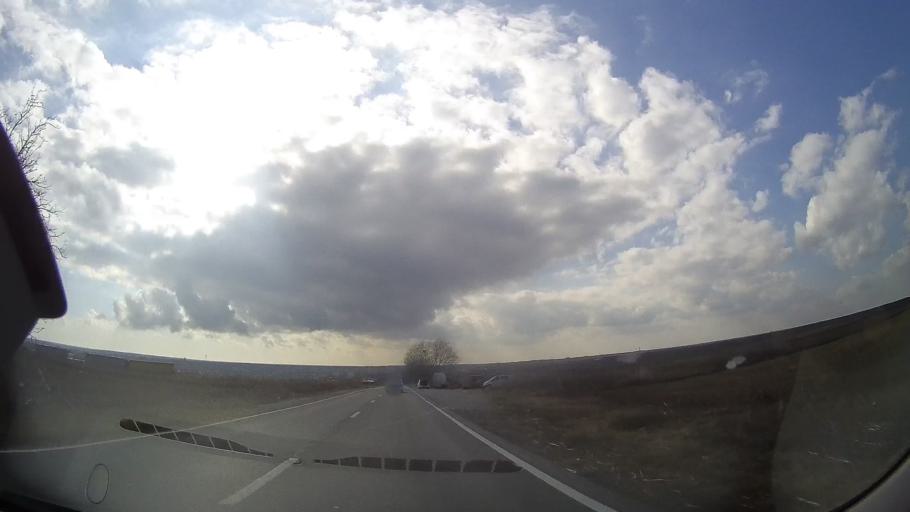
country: RO
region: Constanta
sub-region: Oras Techirghiol
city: Techirghiol
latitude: 44.0701
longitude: 28.5960
